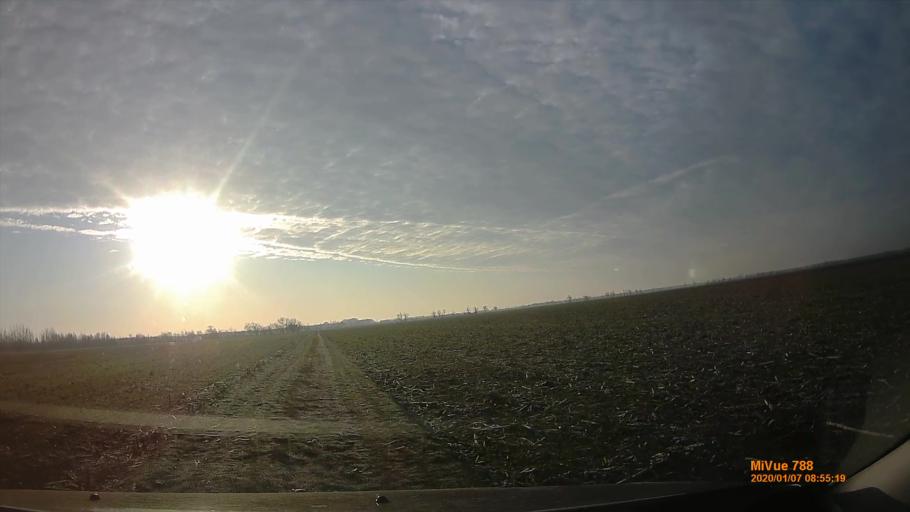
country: HU
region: Gyor-Moson-Sopron
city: Rajka
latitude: 47.9922
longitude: 17.1758
